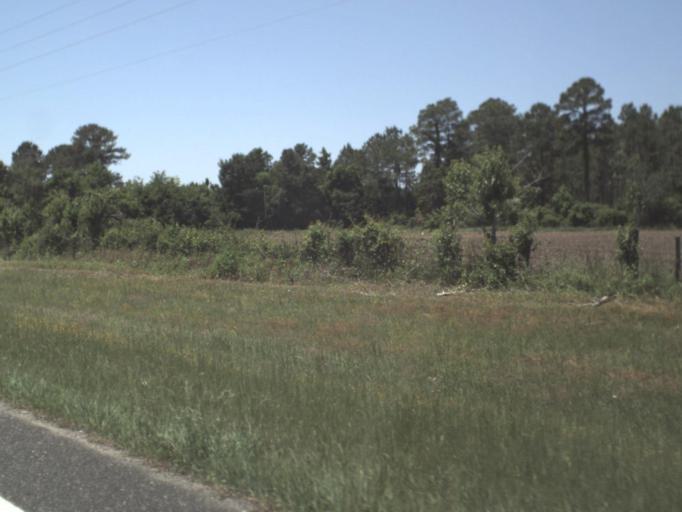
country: US
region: Florida
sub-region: Jefferson County
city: Monticello
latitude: 30.4457
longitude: -83.9004
